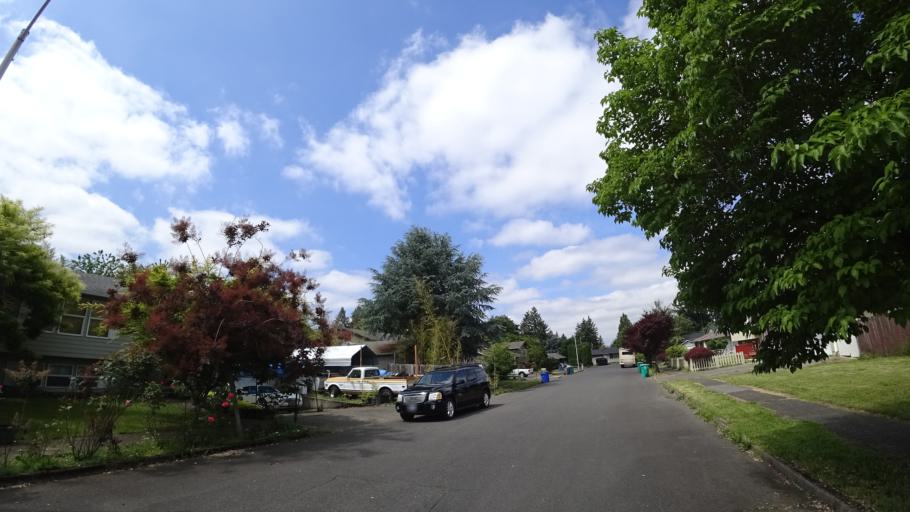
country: US
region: Oregon
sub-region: Multnomah County
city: Gresham
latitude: 45.4949
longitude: -122.4863
